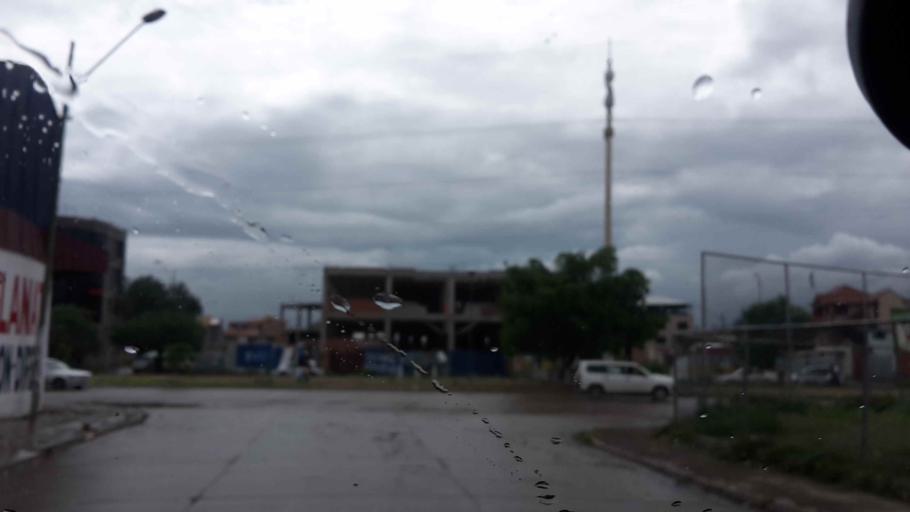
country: BO
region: Cochabamba
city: Cochabamba
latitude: -17.3982
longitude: -66.1853
